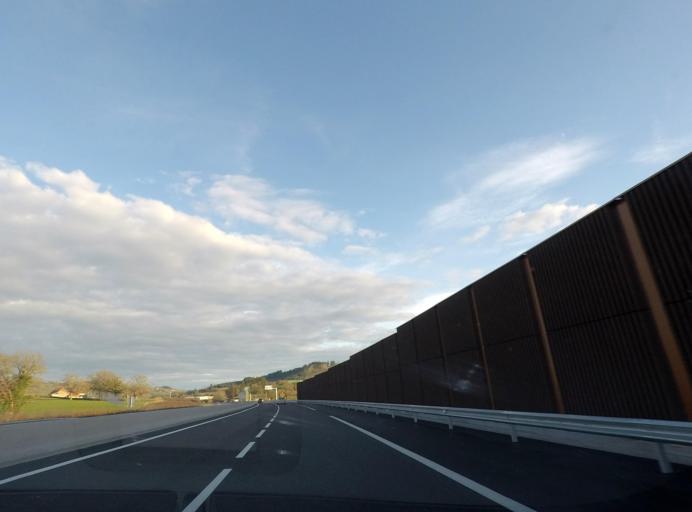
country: FR
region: Bourgogne
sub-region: Departement de Saone-et-Loire
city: Matour
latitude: 46.3783
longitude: 4.4940
